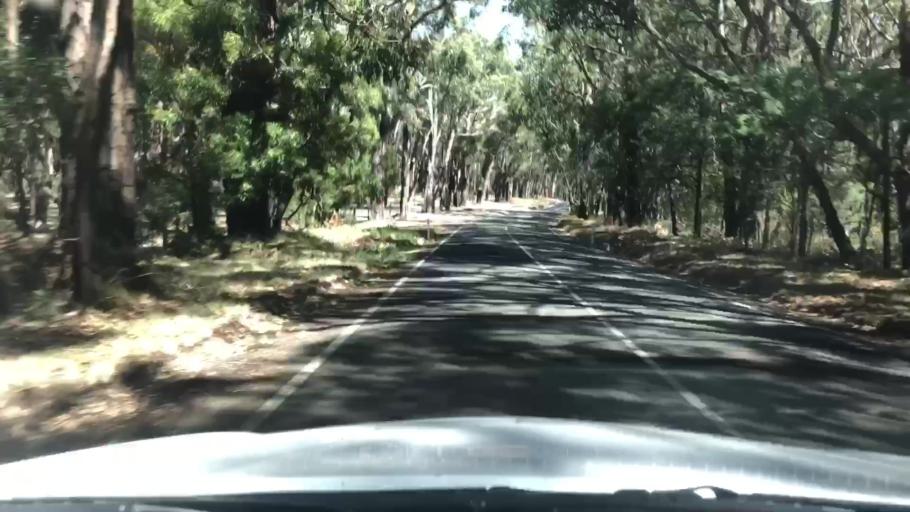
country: AU
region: Victoria
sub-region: Yarra Ranges
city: Macclesfield
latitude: -37.8346
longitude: 145.4876
